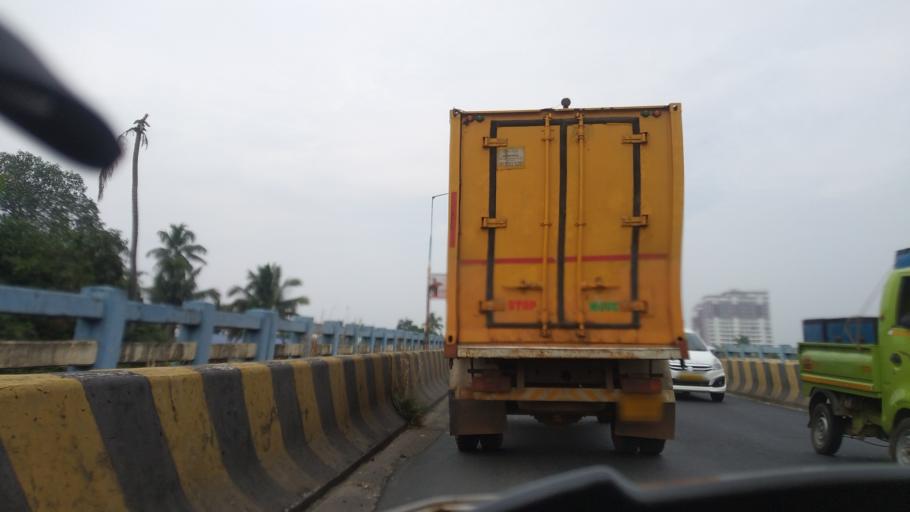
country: IN
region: Kerala
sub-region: Ernakulam
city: Elur
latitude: 10.0338
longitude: 76.3038
